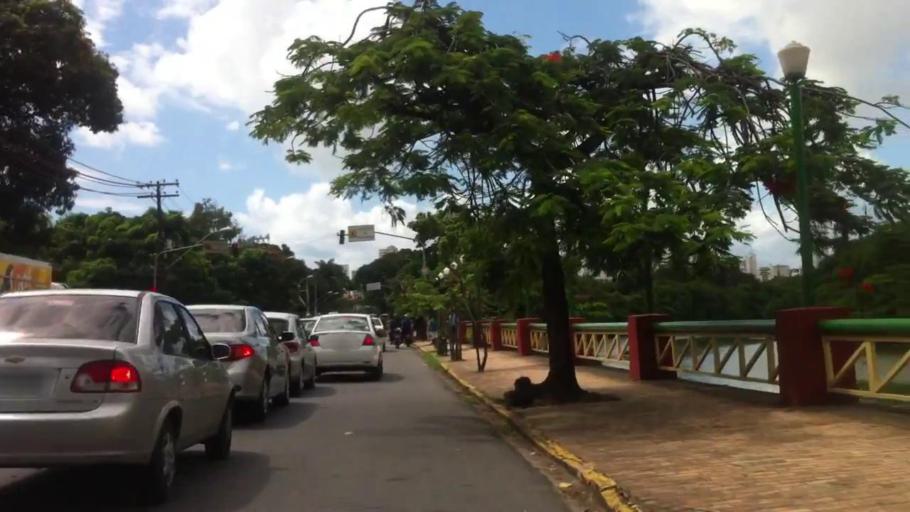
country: BR
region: Pernambuco
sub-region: Recife
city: Recife
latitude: -8.0386
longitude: -34.9052
